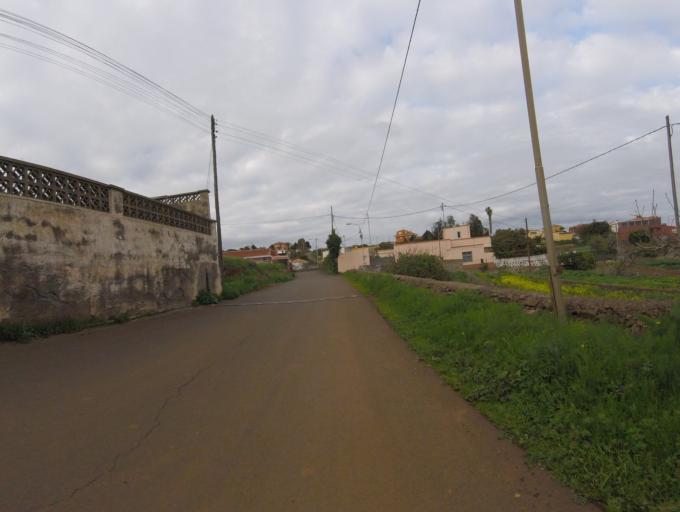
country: ES
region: Canary Islands
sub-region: Provincia de Santa Cruz de Tenerife
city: La Laguna
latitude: 28.4464
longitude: -16.3353
